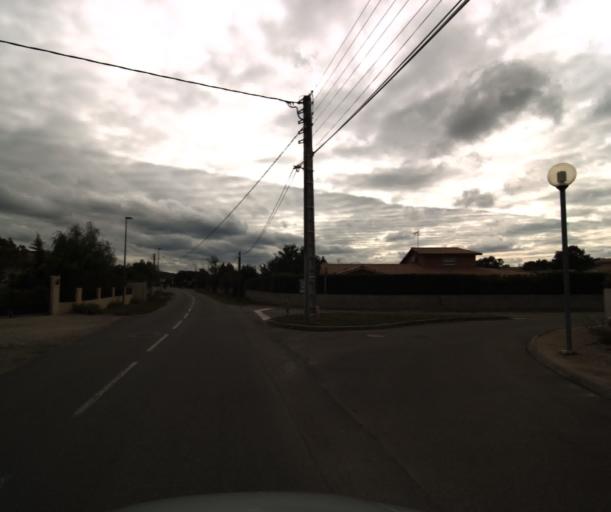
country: FR
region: Midi-Pyrenees
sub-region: Departement de la Haute-Garonne
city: Eaunes
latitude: 43.4325
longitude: 1.3609
